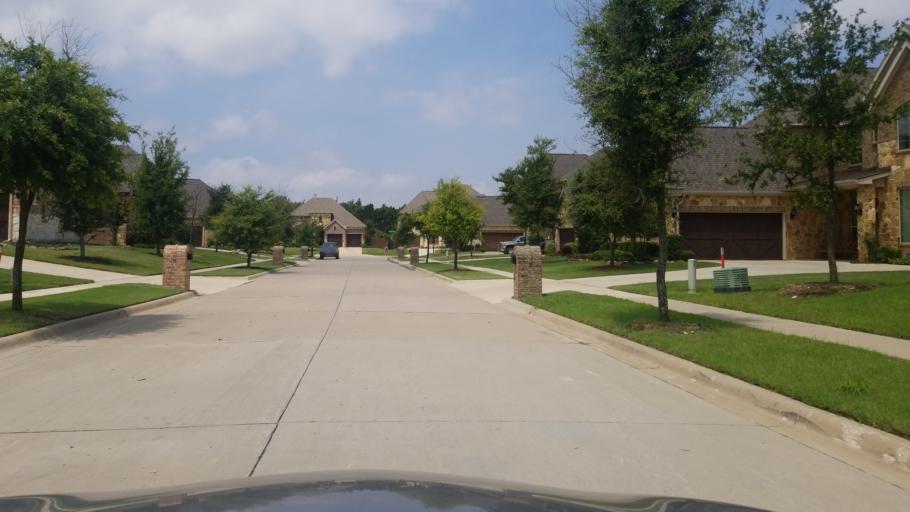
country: US
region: Texas
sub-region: Dallas County
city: Duncanville
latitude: 32.6826
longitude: -96.9377
